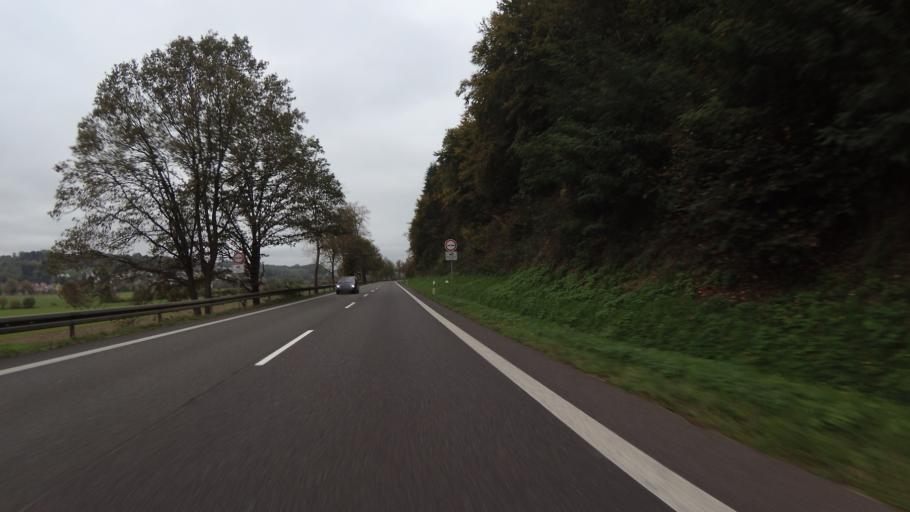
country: DE
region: Saarland
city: Blieskastel
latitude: 49.2553
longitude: 7.2823
